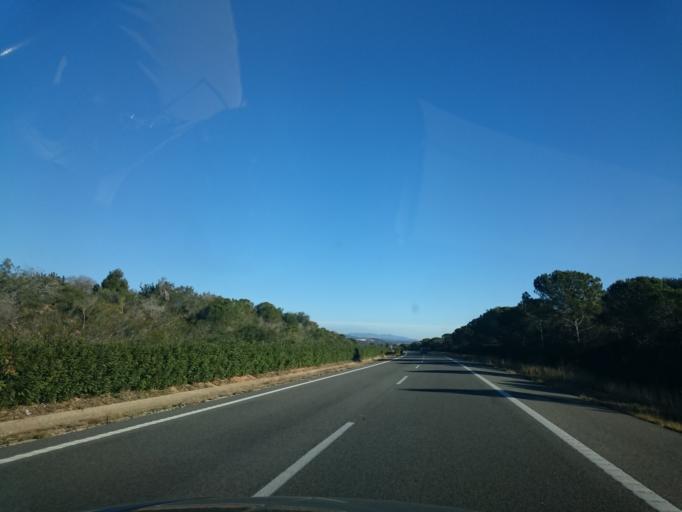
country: ES
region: Catalonia
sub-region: Provincia de Tarragona
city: Masdenverge
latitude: 40.7055
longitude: 0.5494
